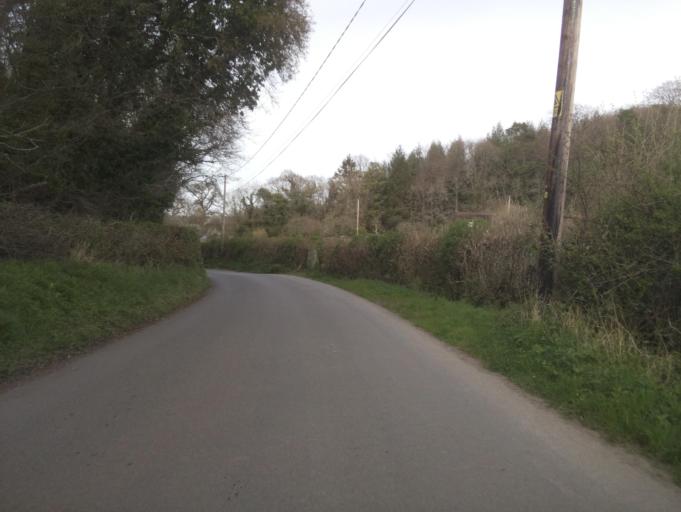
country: GB
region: England
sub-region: Somerset
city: Milborne Port
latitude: 50.9483
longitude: -2.4616
